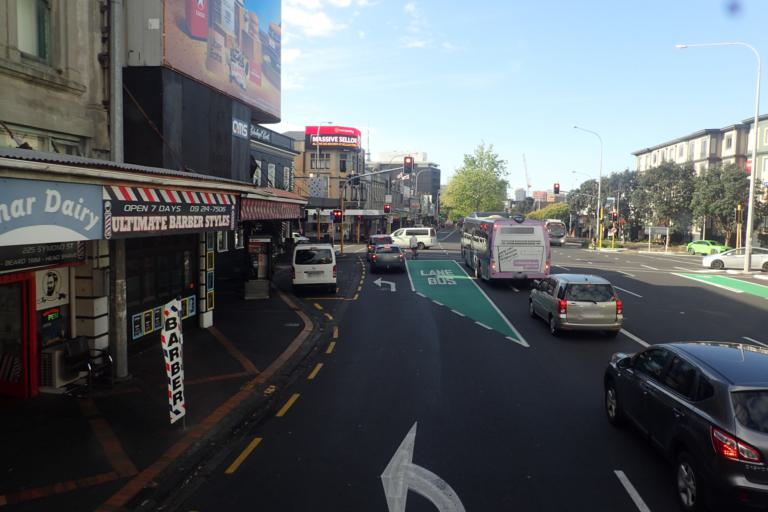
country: NZ
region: Auckland
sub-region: Auckland
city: Auckland
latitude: -36.8642
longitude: 174.7608
